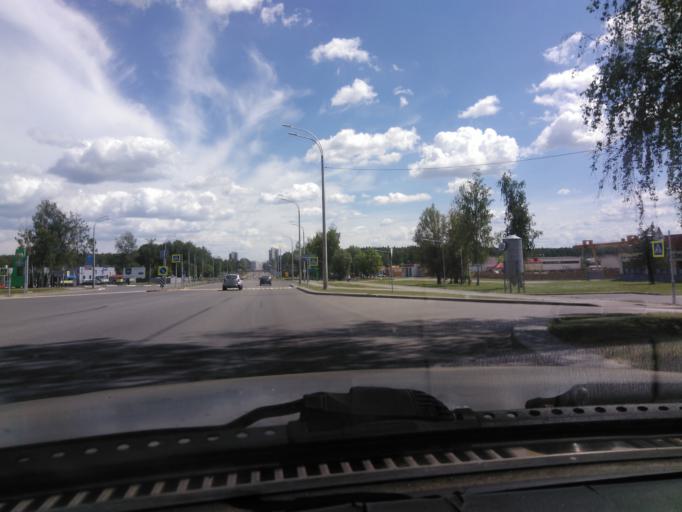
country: BY
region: Mogilev
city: Buynichy
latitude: 53.9287
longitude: 30.2671
